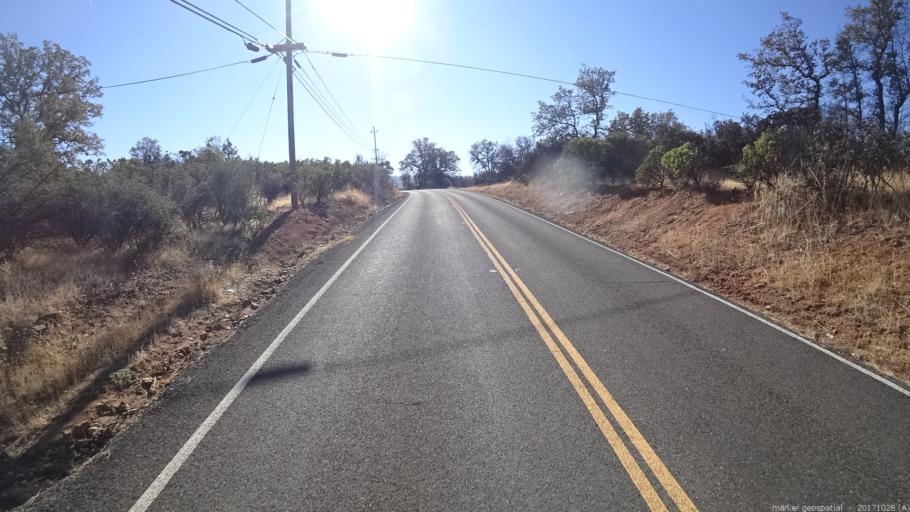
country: US
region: California
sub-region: Shasta County
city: Shasta
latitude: 40.6085
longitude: -122.4618
